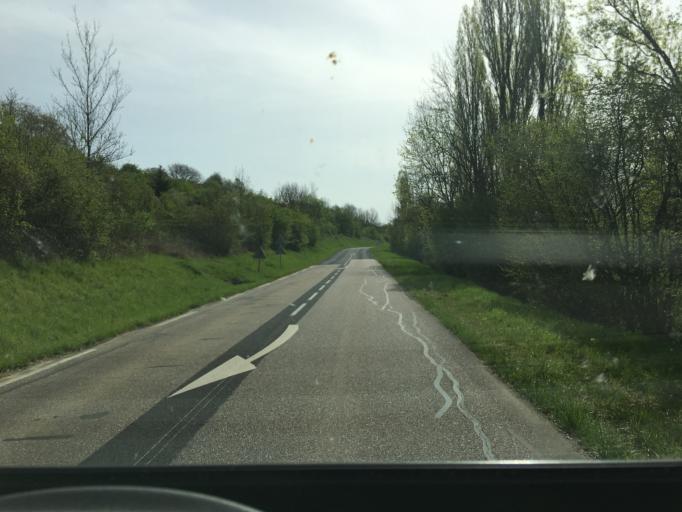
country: FR
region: Lorraine
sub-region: Departement de Meurthe-et-Moselle
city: Chaligny
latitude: 48.6253
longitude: 6.0681
